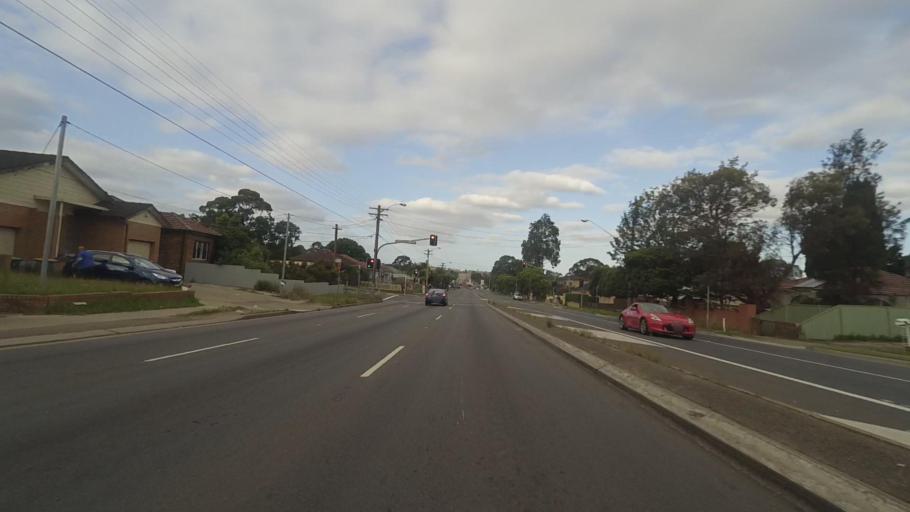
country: AU
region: New South Wales
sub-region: Bankstown
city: Revesby
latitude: -33.9353
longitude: 151.0242
